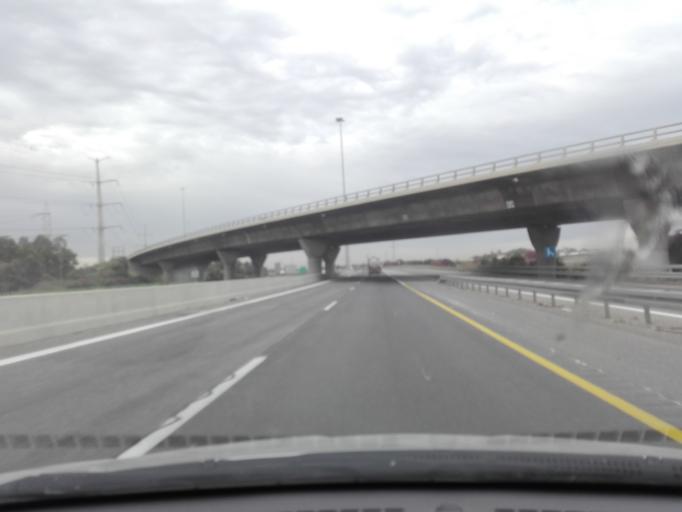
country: IL
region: Central District
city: Ramla
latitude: 31.9071
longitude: 34.8917
